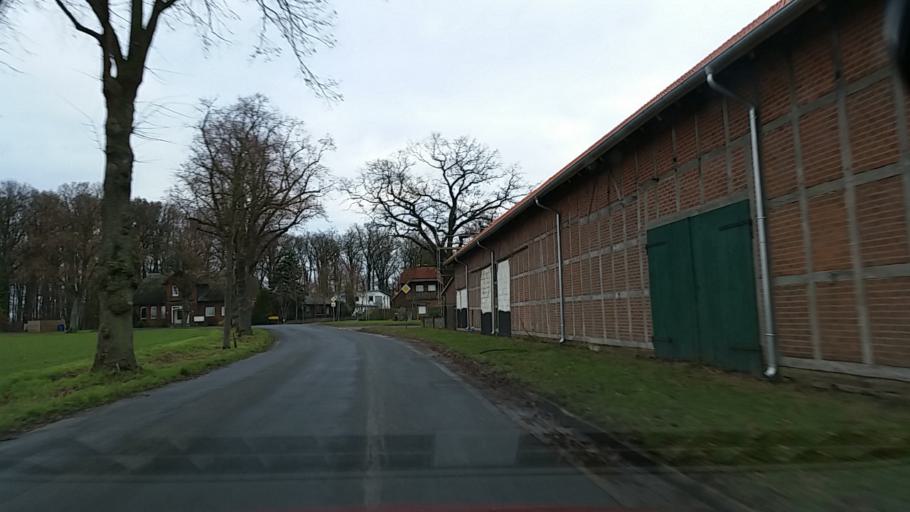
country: DE
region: Lower Saxony
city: Wittingen
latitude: 52.7081
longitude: 10.7467
